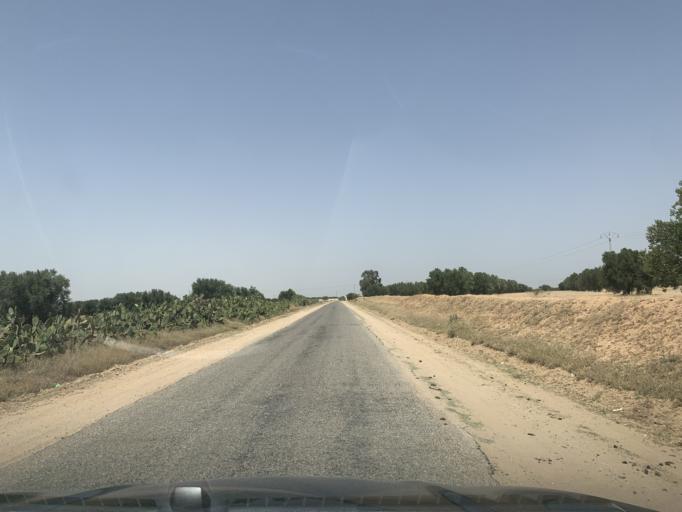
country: TN
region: Al Mahdiyah
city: Shurban
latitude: 35.1787
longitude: 10.2350
